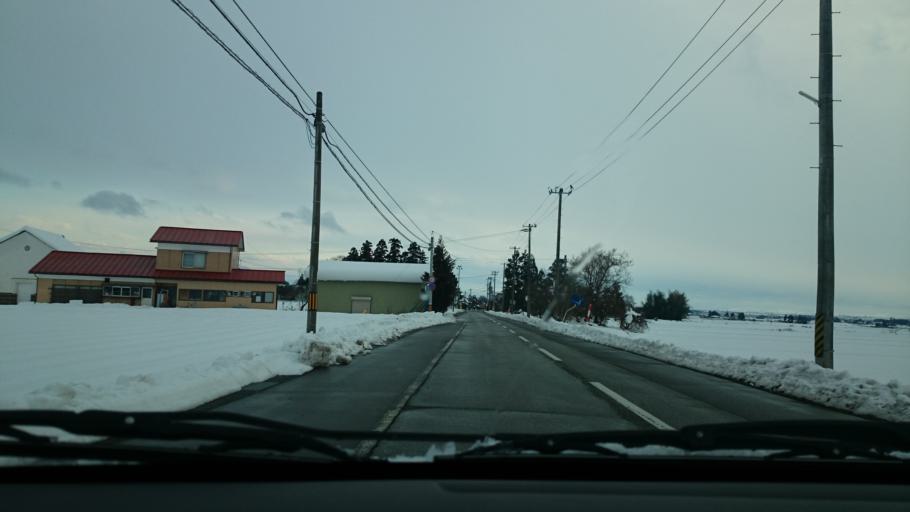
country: JP
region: Fukushima
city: Kitakata
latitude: 37.6369
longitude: 139.9233
